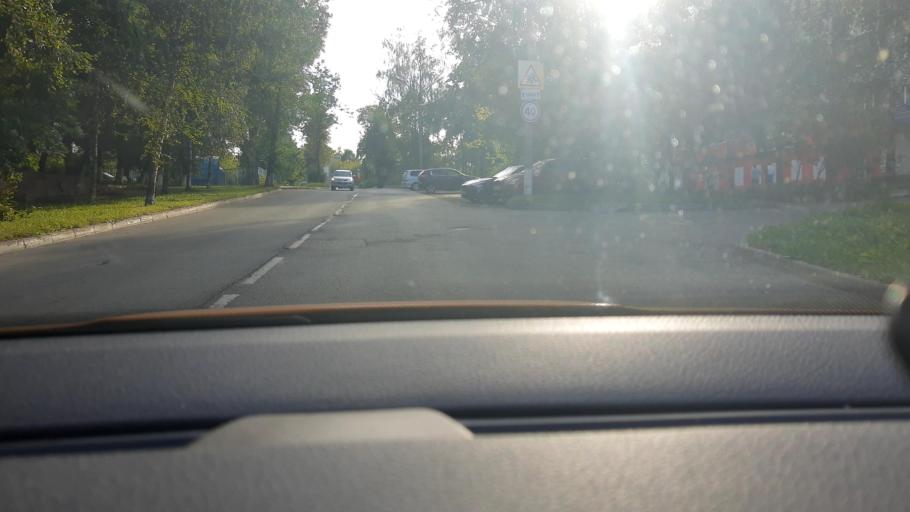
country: RU
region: Moskovskaya
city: Bolshevo
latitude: 55.9497
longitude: 37.8349
